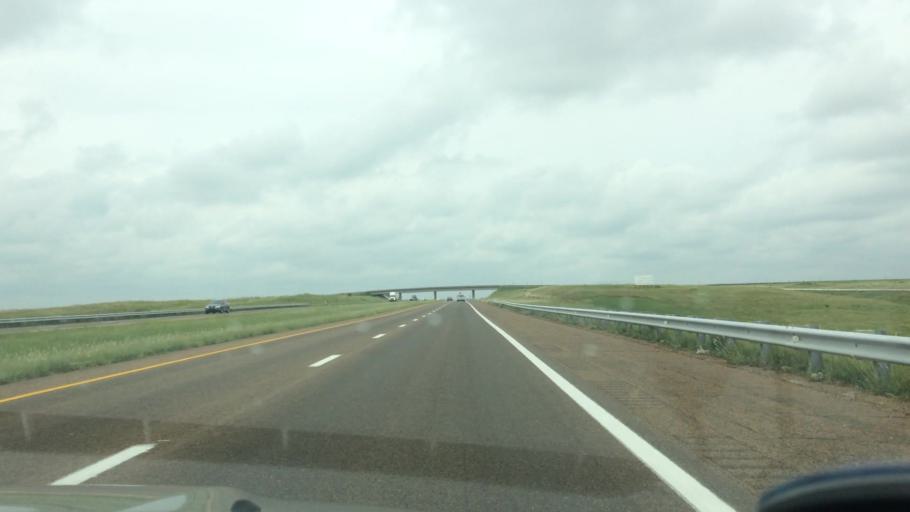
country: US
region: Kansas
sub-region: Ellis County
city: Ellis
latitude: 38.9412
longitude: -99.4927
